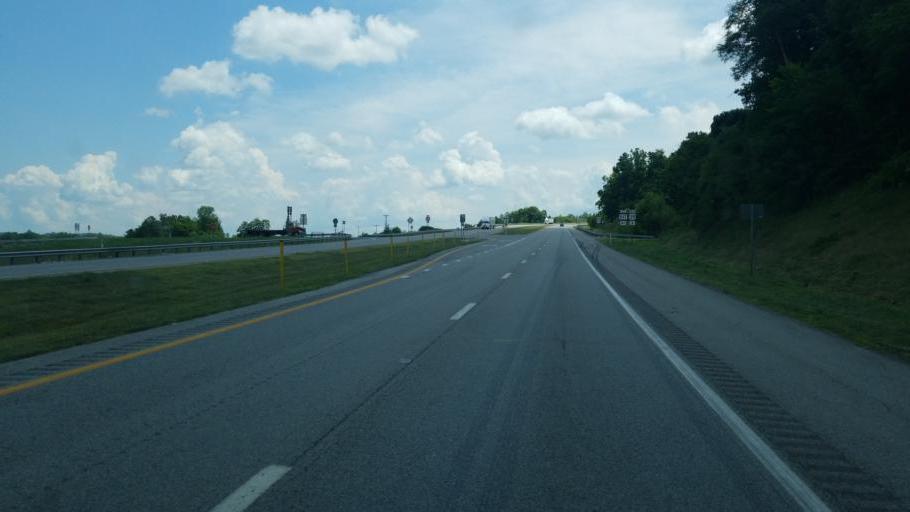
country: US
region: West Virginia
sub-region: Mason County
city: Point Pleasant
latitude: 38.8136
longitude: -82.1107
